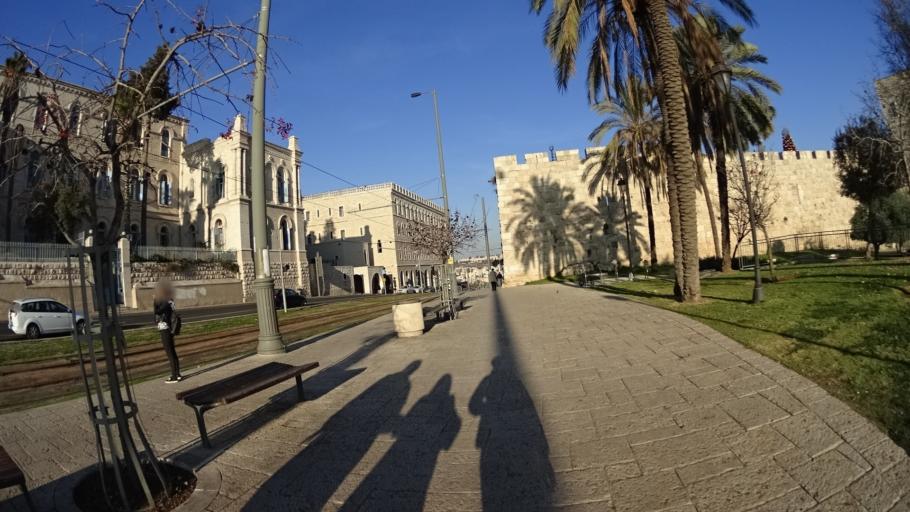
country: IL
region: Jerusalem
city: West Jerusalem
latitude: 31.7790
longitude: 35.2256
